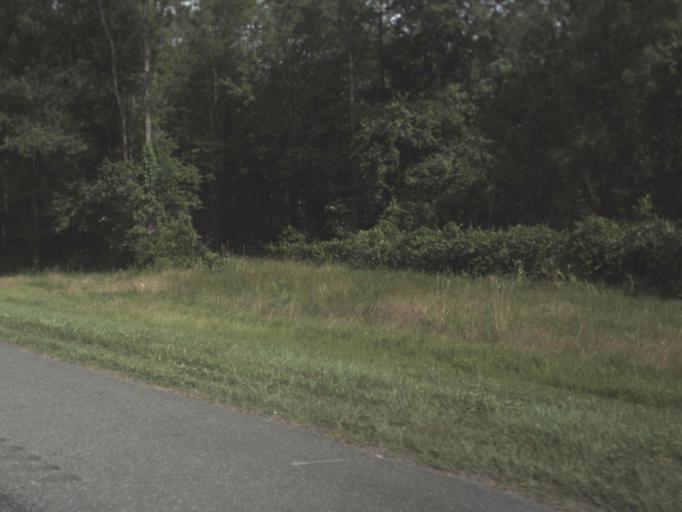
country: US
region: Florida
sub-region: Columbia County
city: Five Points
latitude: 30.2408
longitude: -82.6081
